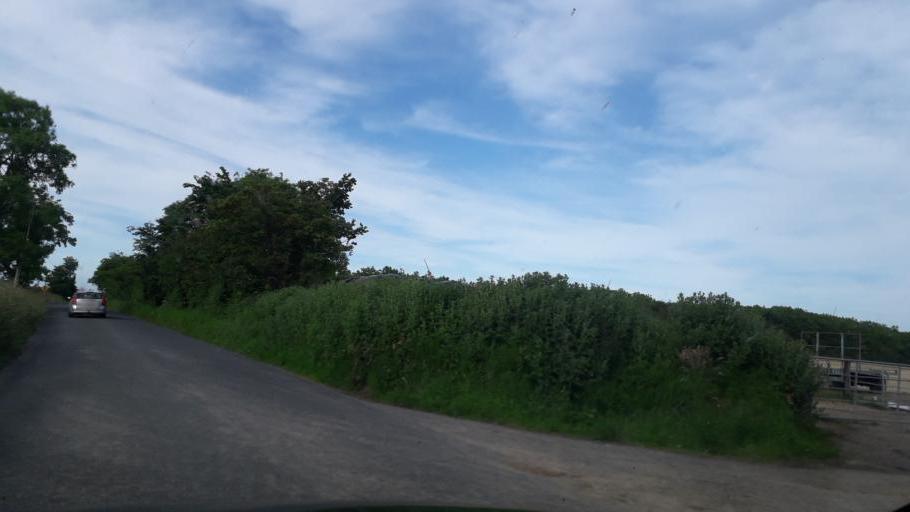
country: IE
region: Leinster
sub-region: Loch Garman
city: Courtown
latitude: 52.5333
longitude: -6.2572
